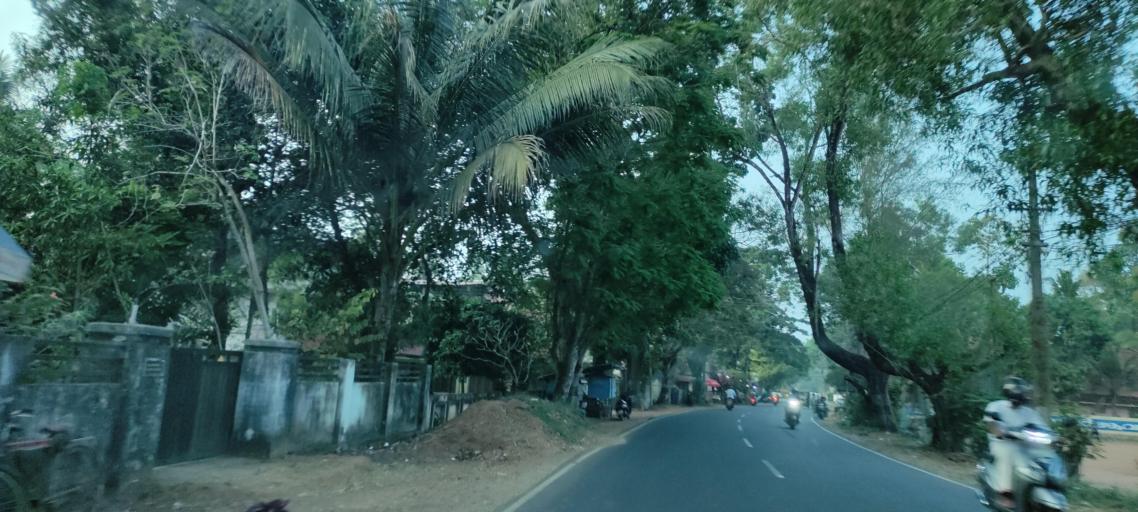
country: IN
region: Kerala
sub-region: Alappuzha
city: Mavelikara
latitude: 9.2824
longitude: 76.5309
